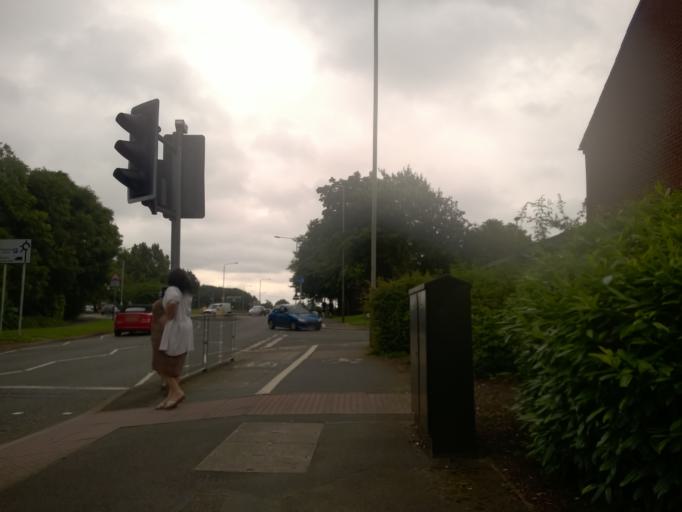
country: GB
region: England
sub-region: Leicestershire
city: Anstey
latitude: 52.6639
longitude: -1.1684
